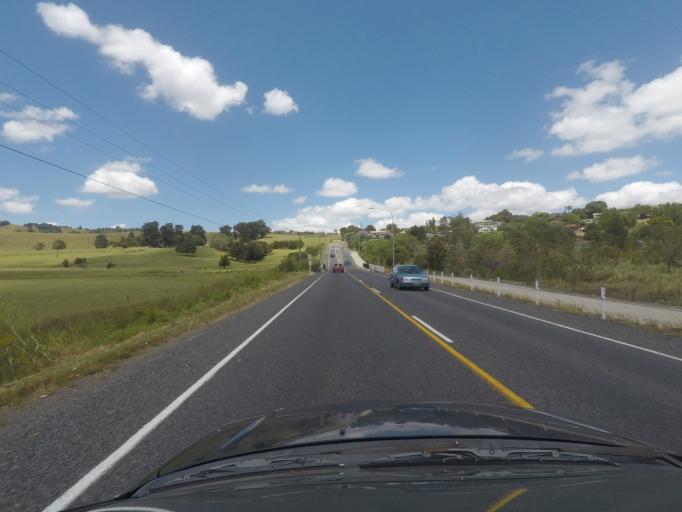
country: NZ
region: Northland
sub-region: Whangarei
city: Whangarei
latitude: -35.7401
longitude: 174.3623
